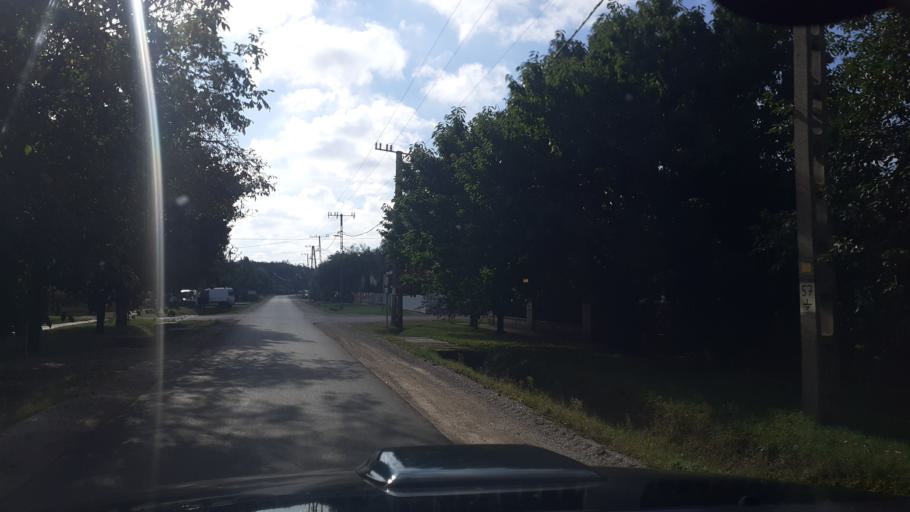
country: HU
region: Fejer
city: dunaujvaros
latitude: 46.9515
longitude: 18.8570
